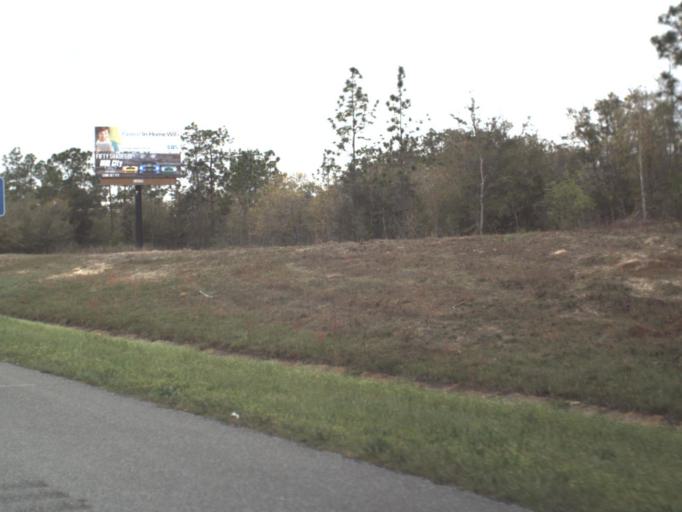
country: US
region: Florida
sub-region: Okaloosa County
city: Crestview
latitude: 30.7270
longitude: -86.5509
